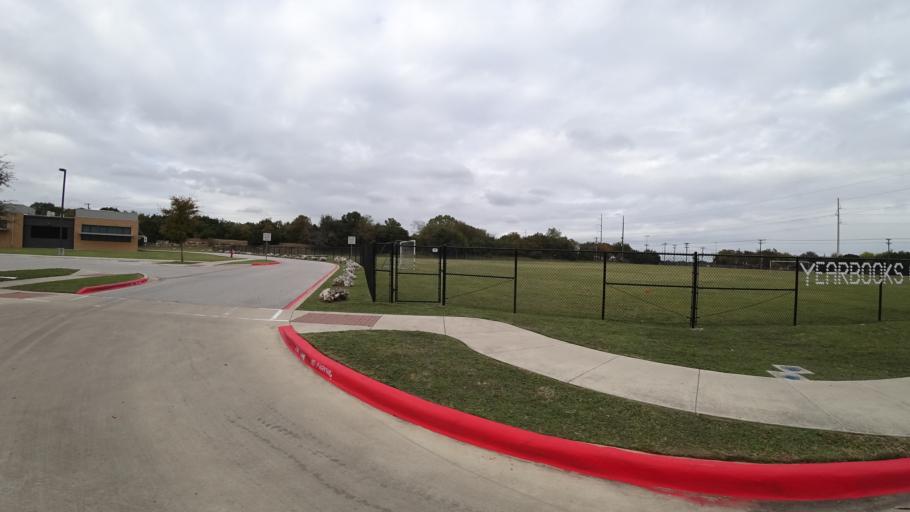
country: US
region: Texas
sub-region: Williamson County
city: Round Rock
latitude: 30.5027
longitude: -97.7006
